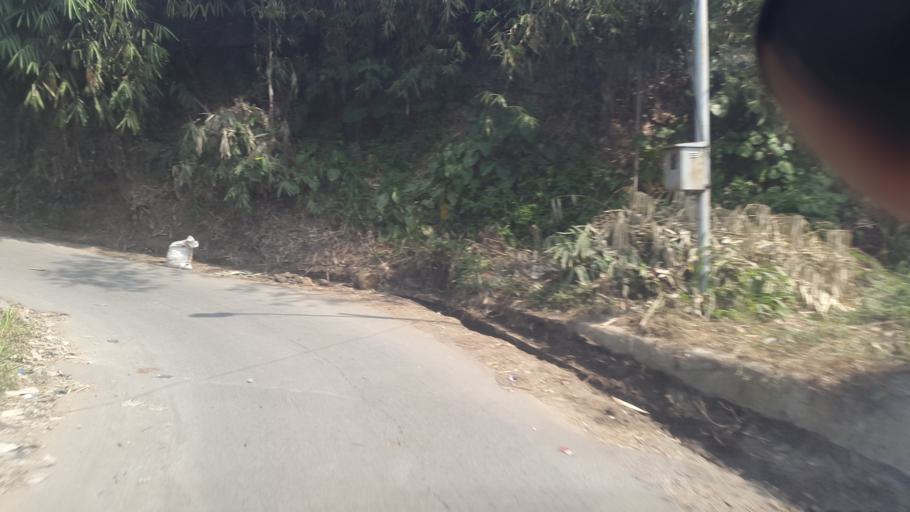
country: ID
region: West Java
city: Sukabumi
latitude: -6.8879
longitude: 106.9192
